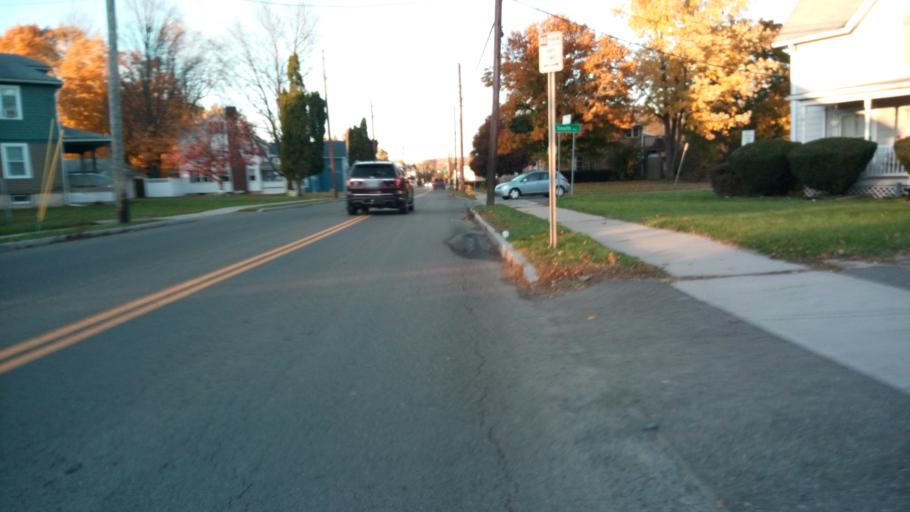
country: US
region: New York
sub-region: Chemung County
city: Southport
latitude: 42.0721
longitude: -76.8136
